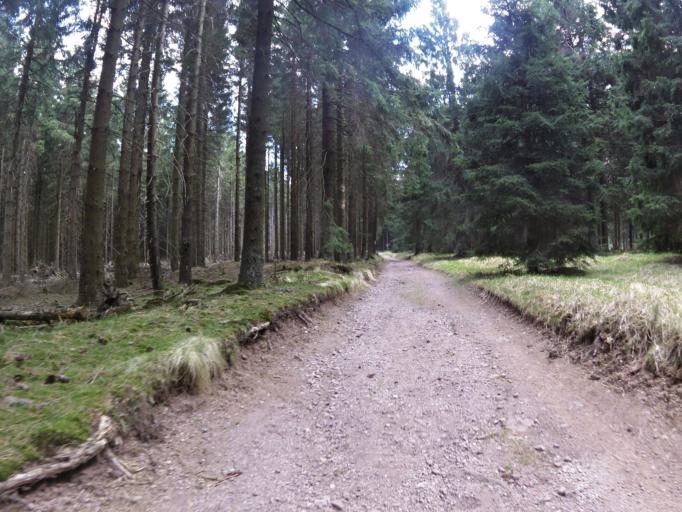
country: DE
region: Thuringia
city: Unterschonau
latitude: 50.7523
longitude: 10.5686
